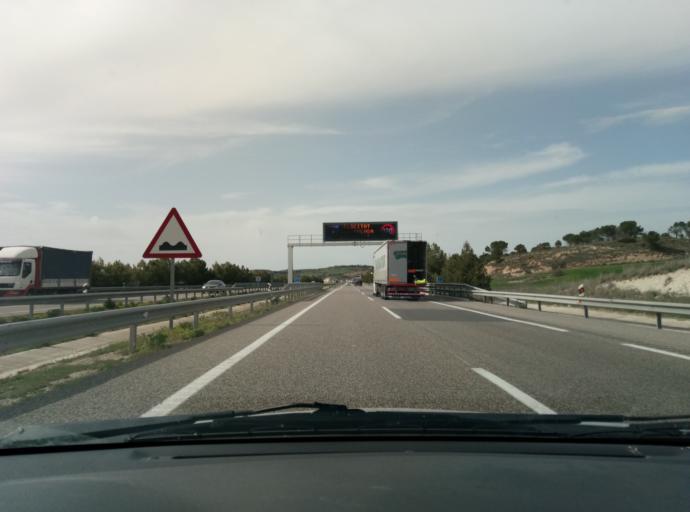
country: ES
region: Catalonia
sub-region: Provincia de Lleida
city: Cervera
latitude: 41.6541
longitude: 1.3142
